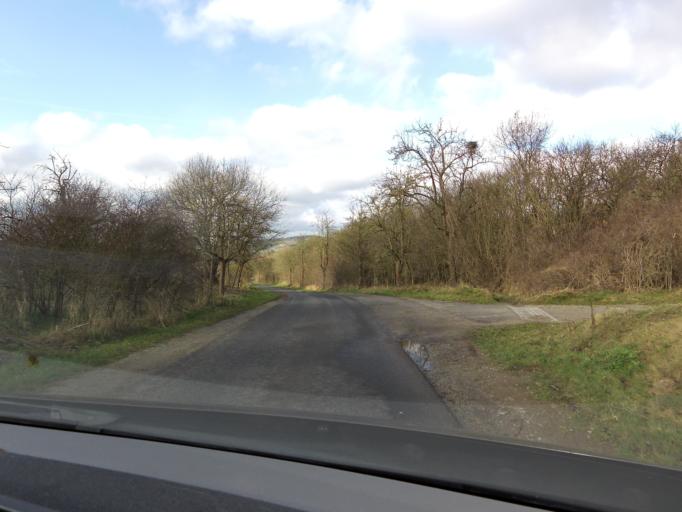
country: DE
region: Thuringia
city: Creuzburg
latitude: 51.0446
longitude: 10.2582
